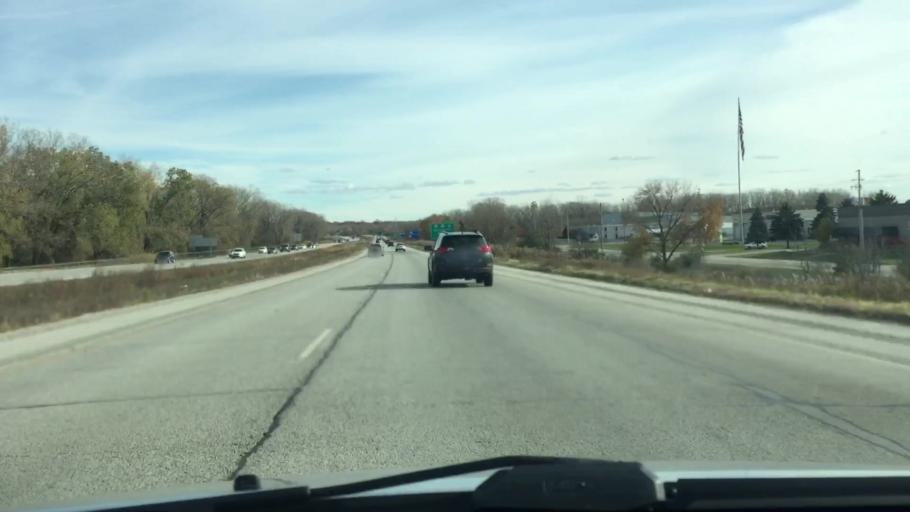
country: US
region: Wisconsin
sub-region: Brown County
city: Green Bay
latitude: 44.5249
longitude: -87.9831
